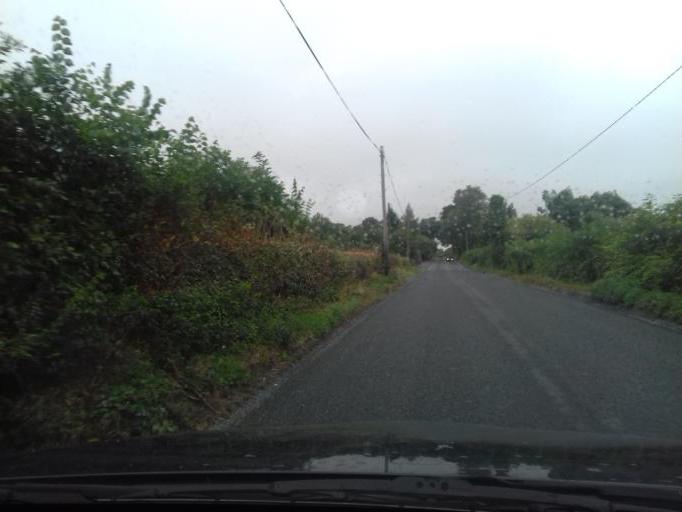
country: IE
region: Leinster
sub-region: Kilkenny
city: Graiguenamanagh
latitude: 52.6125
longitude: -6.9369
